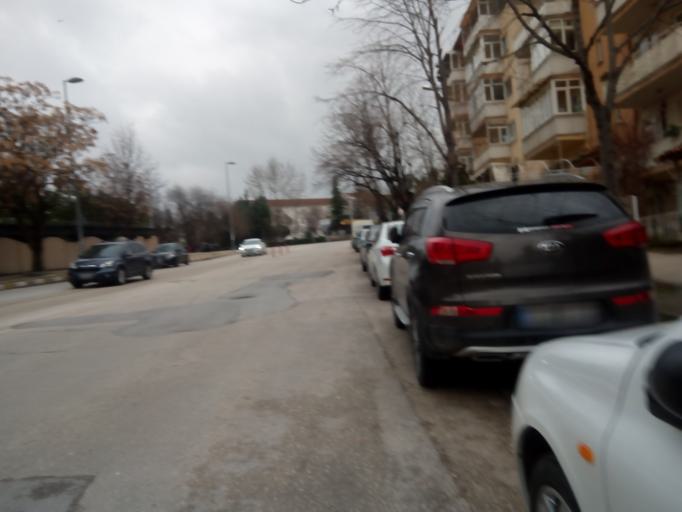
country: TR
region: Bursa
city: Niluefer
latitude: 40.2499
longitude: 28.9625
